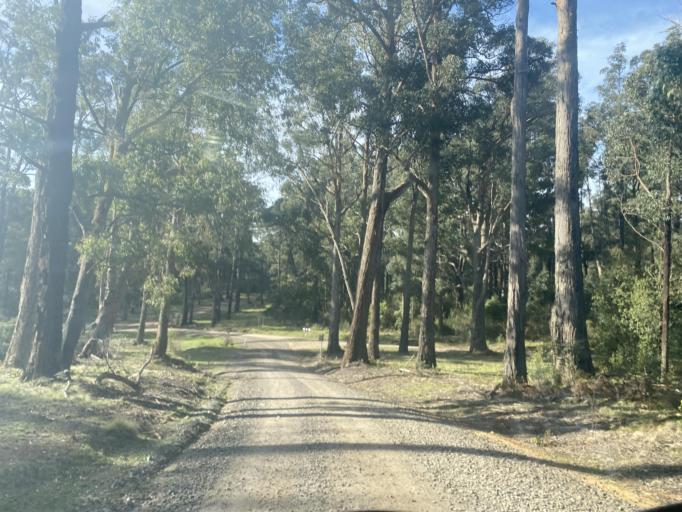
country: AU
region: Victoria
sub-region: Mansfield
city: Mansfield
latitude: -36.8492
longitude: 146.1809
